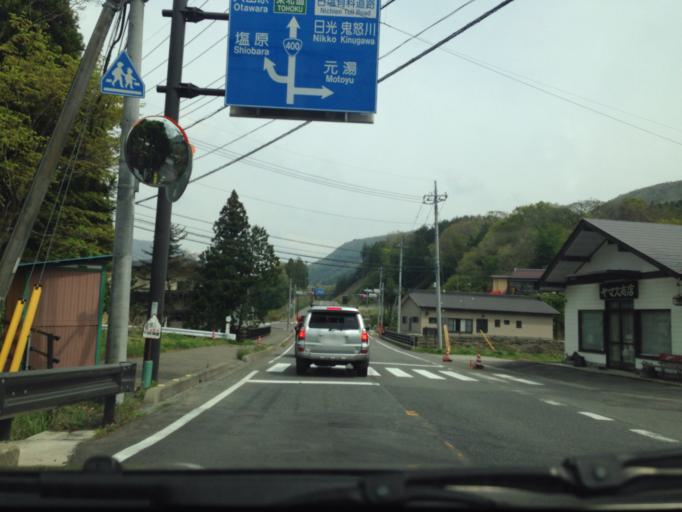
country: JP
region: Tochigi
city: Yaita
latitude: 36.9816
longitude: 139.7881
